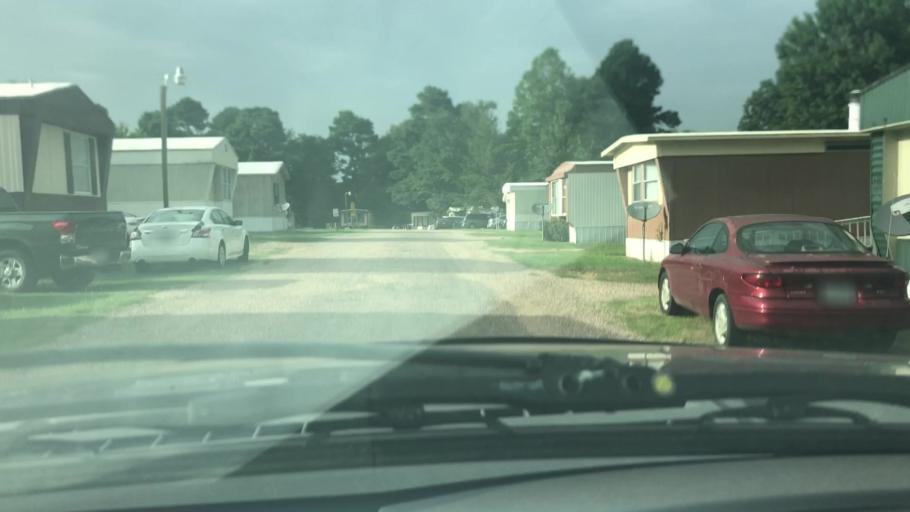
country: US
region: Texas
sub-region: Bowie County
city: Wake Village
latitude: 33.3766
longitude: -94.0945
